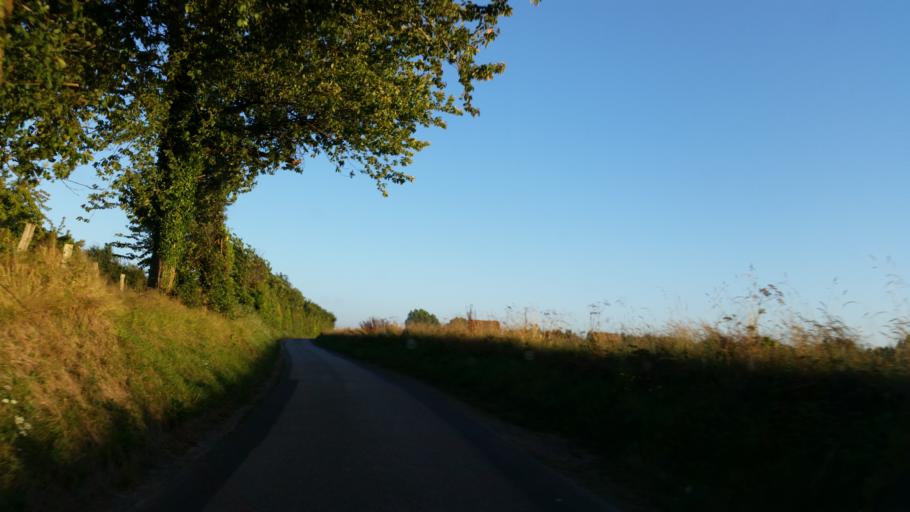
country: FR
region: Lower Normandy
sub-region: Departement du Calvados
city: Equemauville
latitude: 49.3767
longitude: 0.2286
